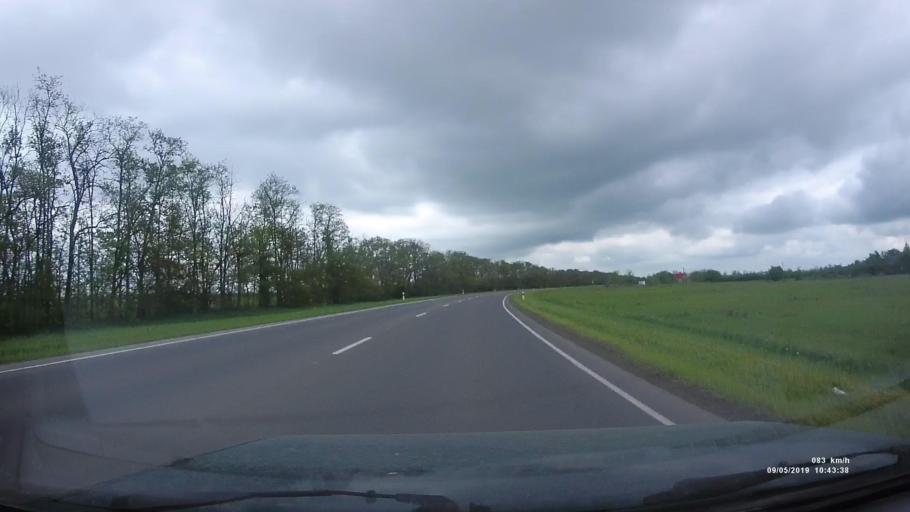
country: RU
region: Rostov
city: Peshkovo
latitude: 47.0063
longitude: 39.4014
